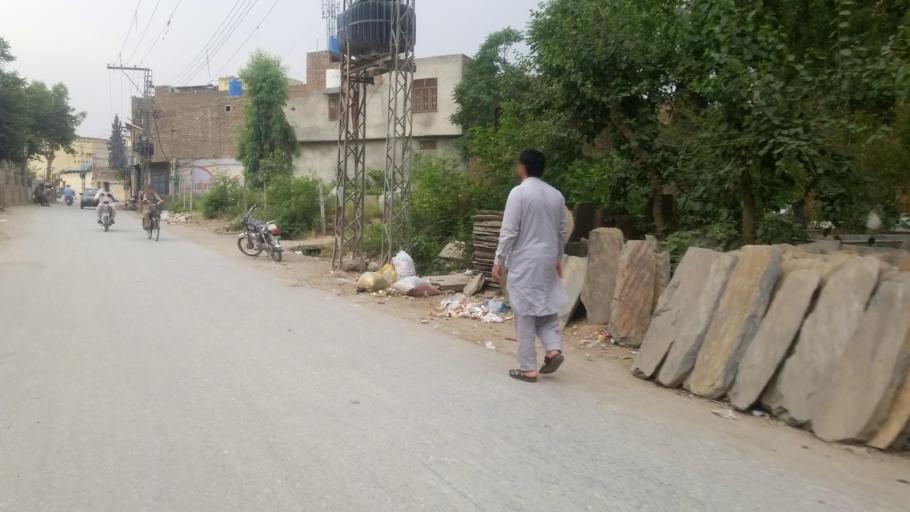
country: PK
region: Khyber Pakhtunkhwa
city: Peshawar
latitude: 33.9953
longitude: 71.5624
